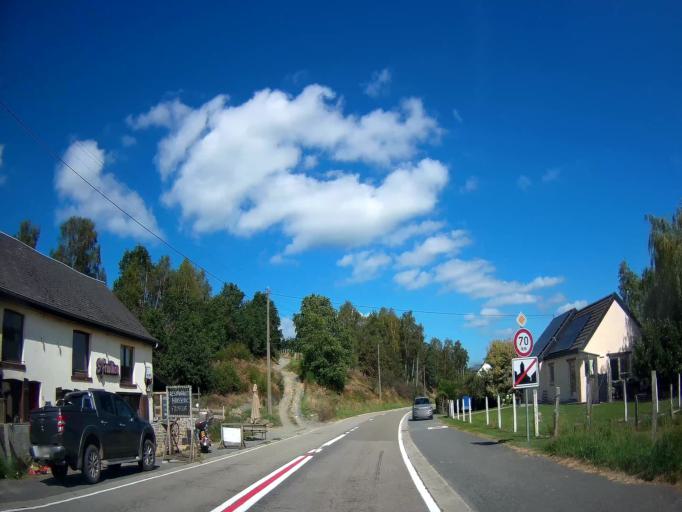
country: BE
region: Wallonia
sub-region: Province du Luxembourg
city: Bertogne
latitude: 50.0874
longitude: 5.6701
